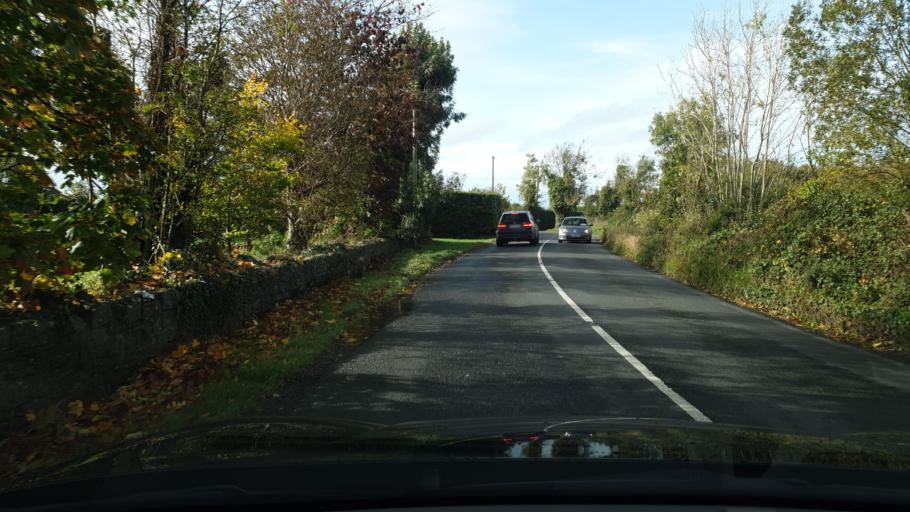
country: IE
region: Leinster
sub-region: An Mhi
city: Ashbourne
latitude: 53.5102
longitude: -6.4271
